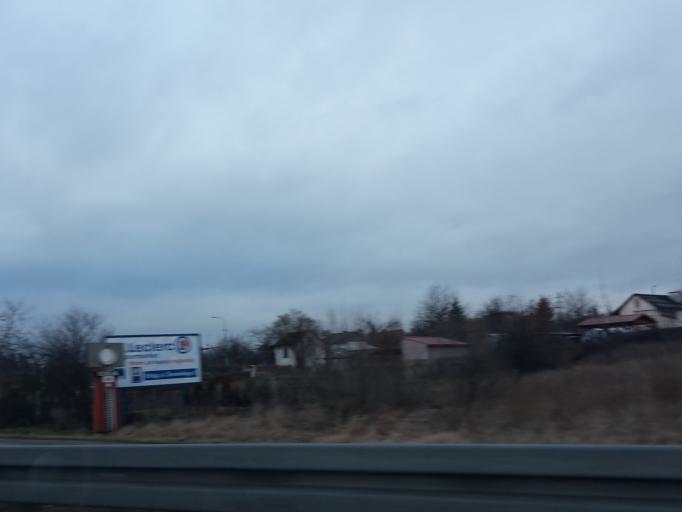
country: PL
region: Warmian-Masurian Voivodeship
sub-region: Powiat elblaski
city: Gronowo Gorne
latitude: 54.1366
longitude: 19.4526
